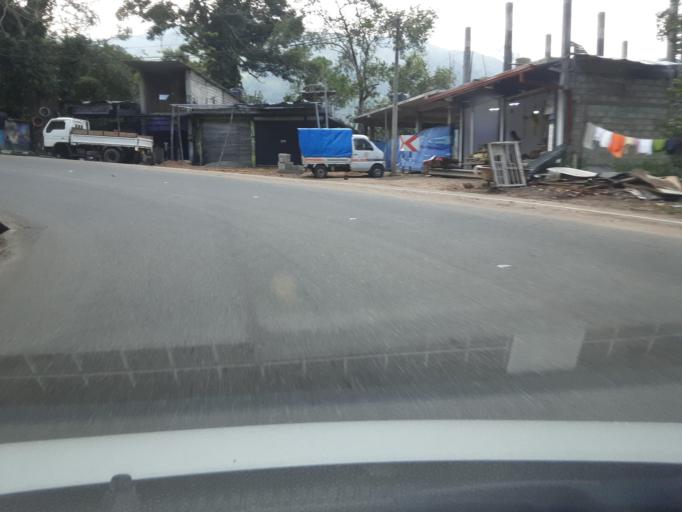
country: LK
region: Uva
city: Badulla
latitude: 6.9543
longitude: 81.0265
